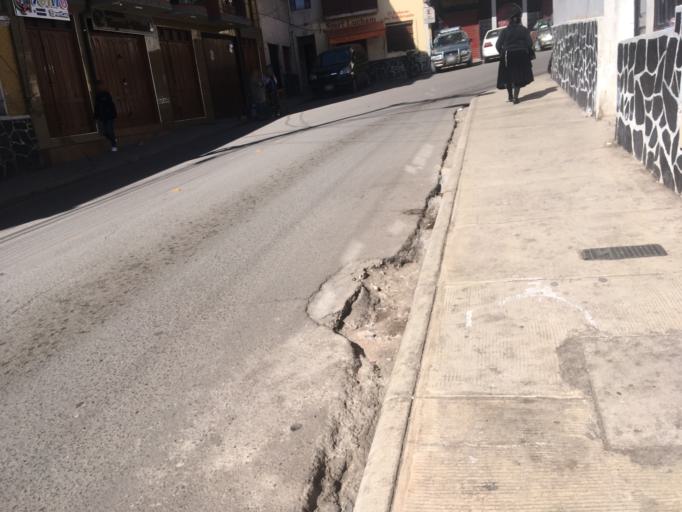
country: BO
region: Potosi
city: Potosi
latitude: -19.5855
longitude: -65.7559
